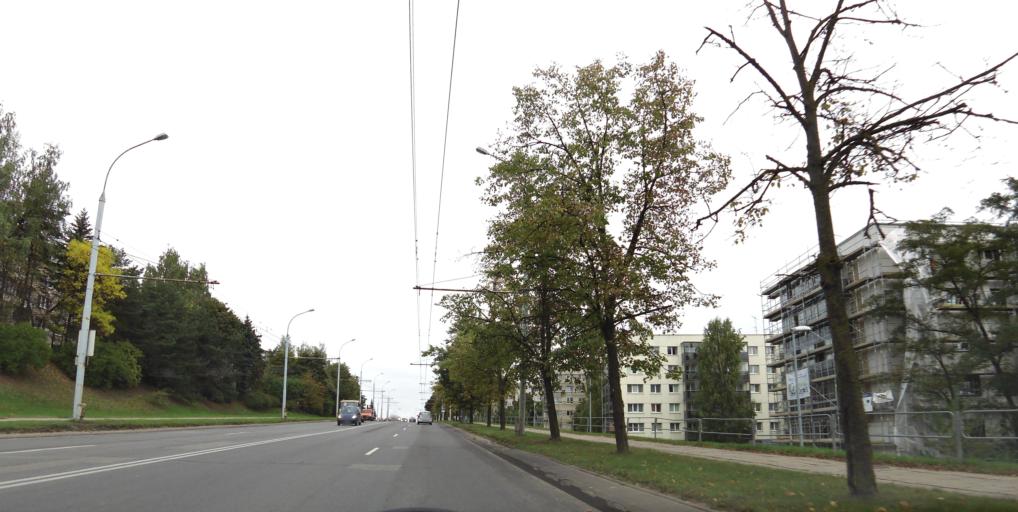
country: LT
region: Vilnius County
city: Rasos
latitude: 54.7086
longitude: 25.3048
